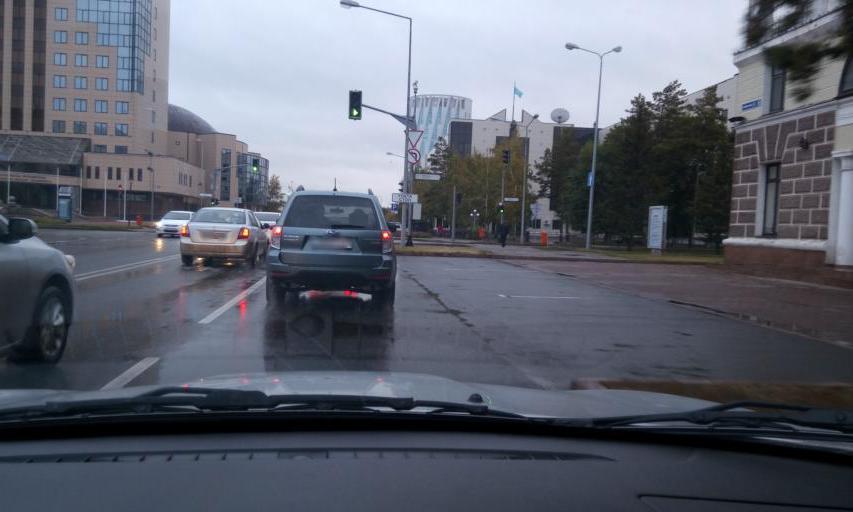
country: KZ
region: Astana Qalasy
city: Astana
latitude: 51.1672
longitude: 71.4211
